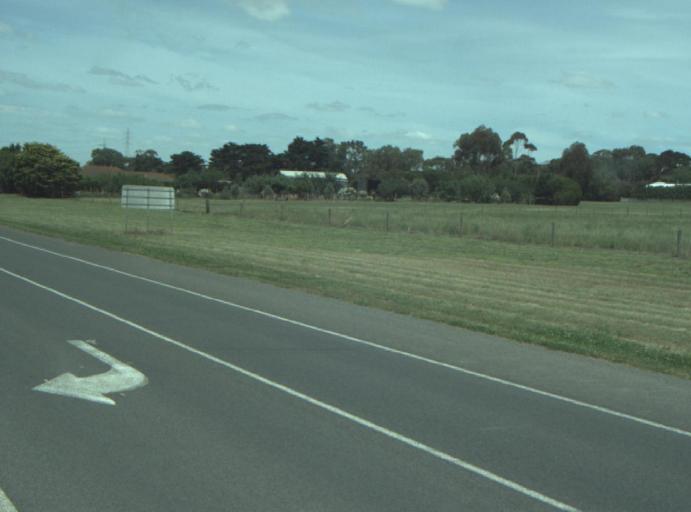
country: AU
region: Victoria
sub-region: Greater Geelong
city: Lara
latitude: -38.0300
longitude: 144.3544
